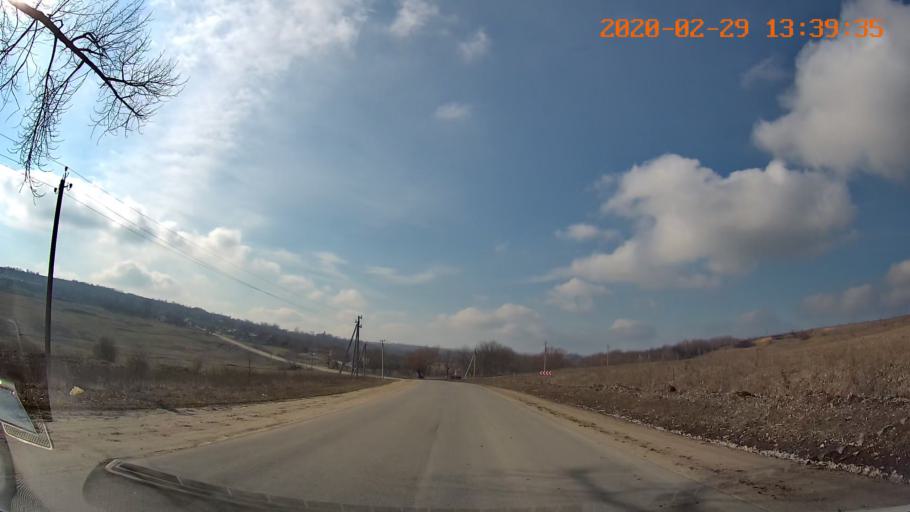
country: MD
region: Floresti
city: Leninskiy
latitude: 47.8515
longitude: 28.5788
